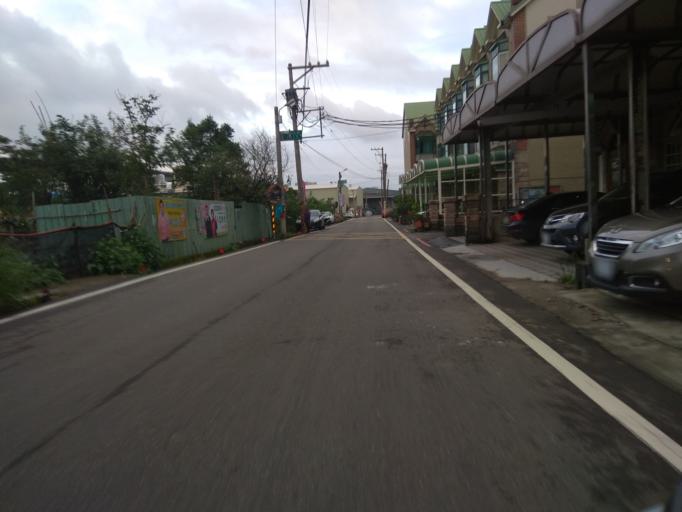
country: TW
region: Taiwan
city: Daxi
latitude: 24.9366
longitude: 121.1931
